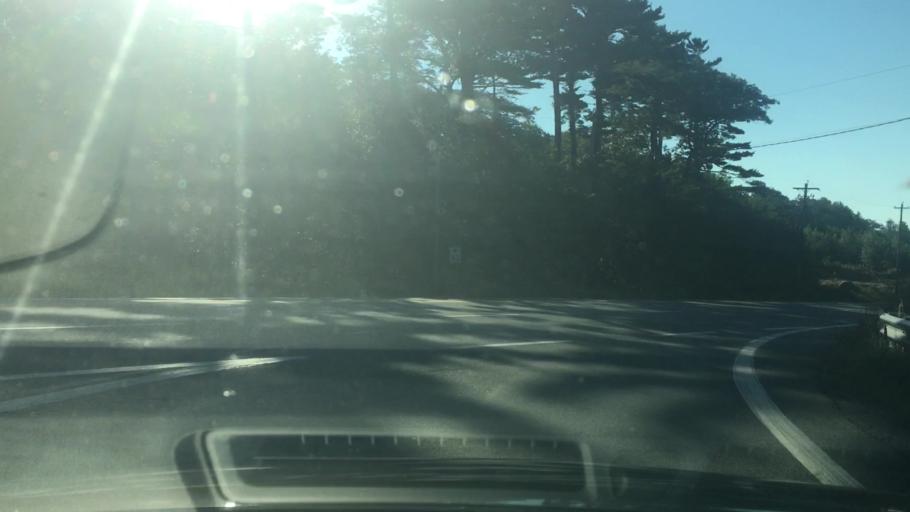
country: CA
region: Nova Scotia
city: Dartmouth
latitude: 44.7427
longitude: -63.6558
